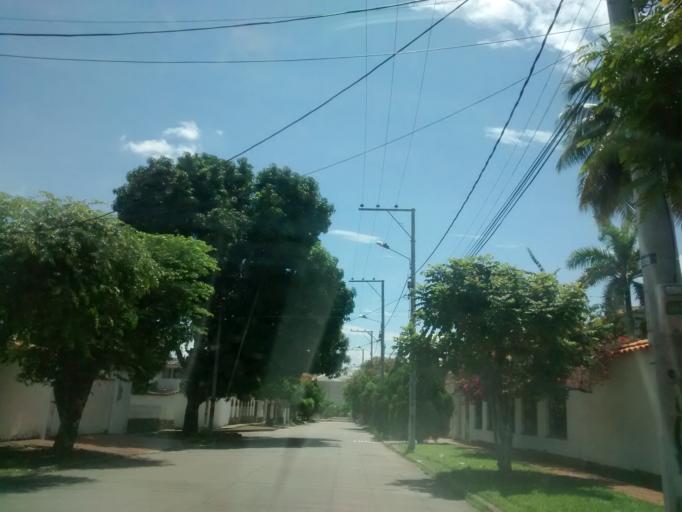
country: CO
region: Cundinamarca
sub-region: Girardot
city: Girardot City
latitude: 4.3064
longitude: -74.7995
